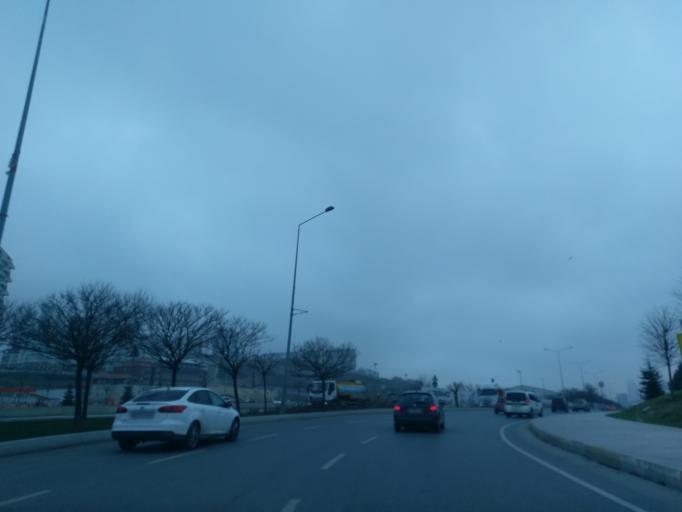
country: TR
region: Istanbul
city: Mahmutbey
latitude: 41.0409
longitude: 28.7738
